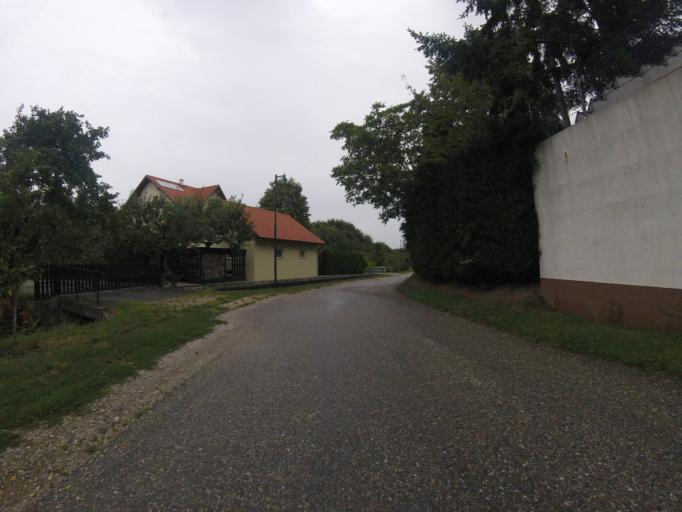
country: AT
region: Burgenland
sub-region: Eisenstadt-Umgebung
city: Donnerskirchen
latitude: 47.9167
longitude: 16.6881
